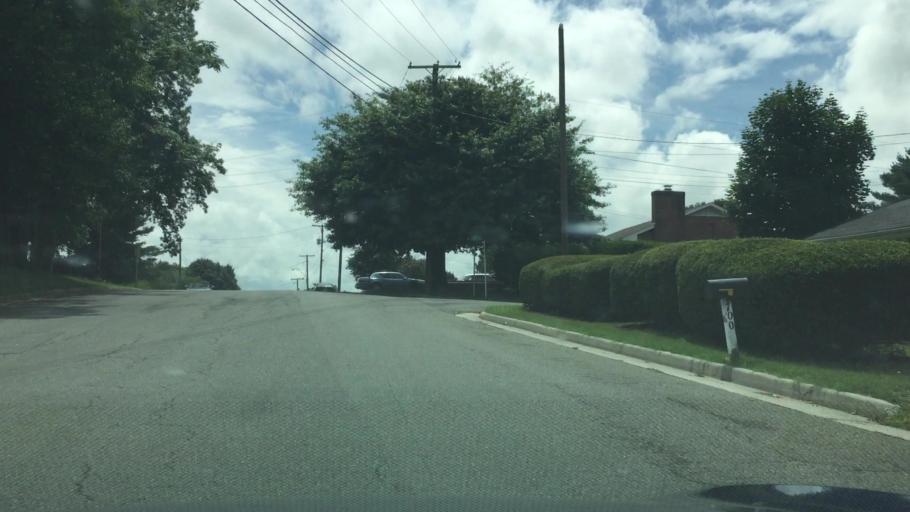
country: US
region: Virginia
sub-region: Wythe County
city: Wytheville
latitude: 36.9477
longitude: -81.0704
